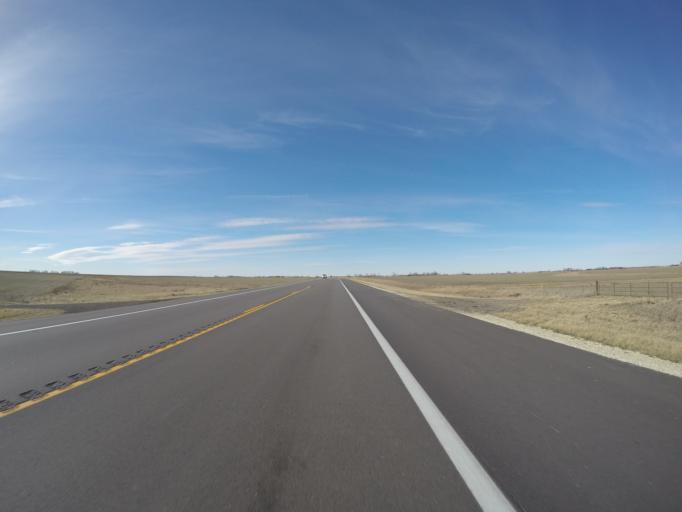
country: US
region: Kansas
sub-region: Marion County
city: Hillsboro
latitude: 38.3668
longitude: -97.3590
